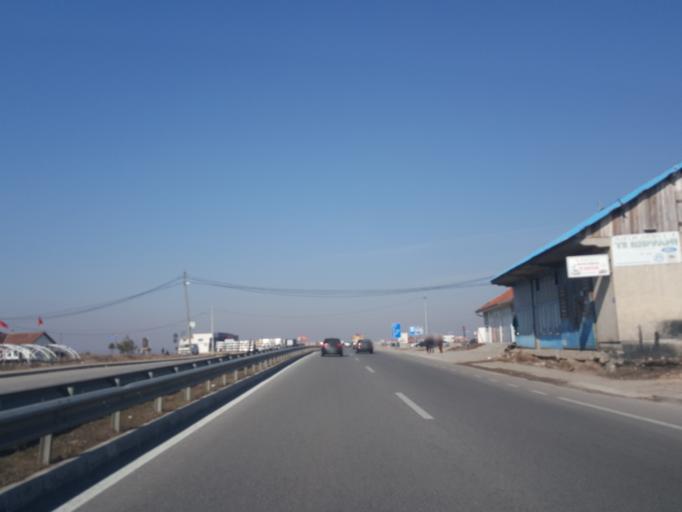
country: XK
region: Pristina
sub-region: Komuna e Obiliqit
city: Obiliq
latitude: 42.7584
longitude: 21.0329
